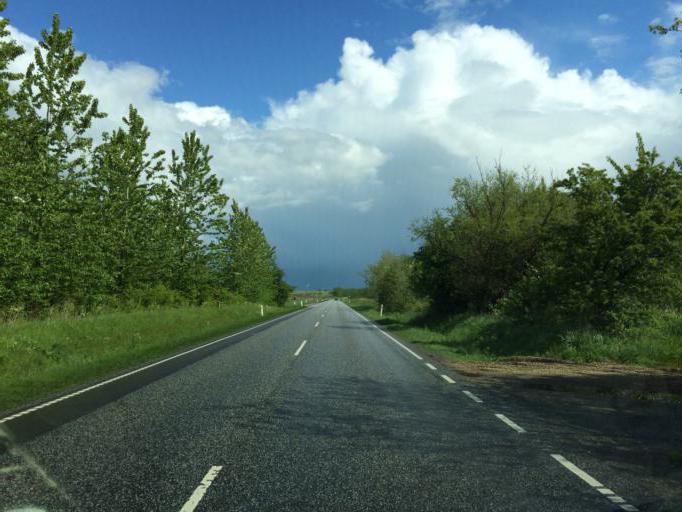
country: DK
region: Central Jutland
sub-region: Holstebro Kommune
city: Vinderup
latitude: 56.4376
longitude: 8.7195
